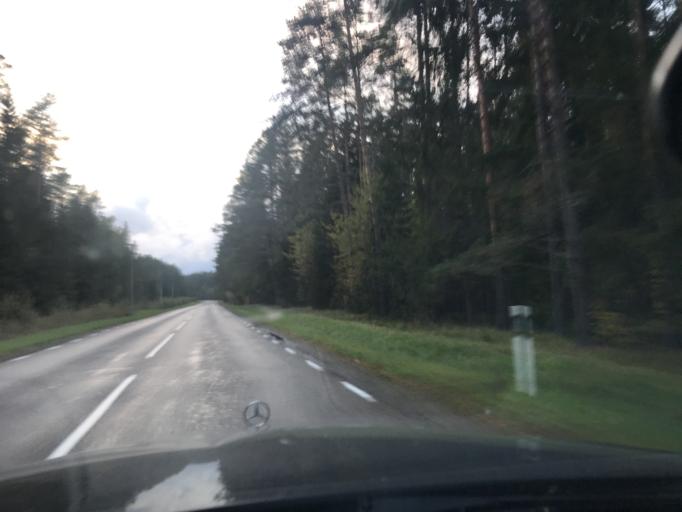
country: EE
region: Valgamaa
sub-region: Torva linn
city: Torva
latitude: 58.0101
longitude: 26.1291
